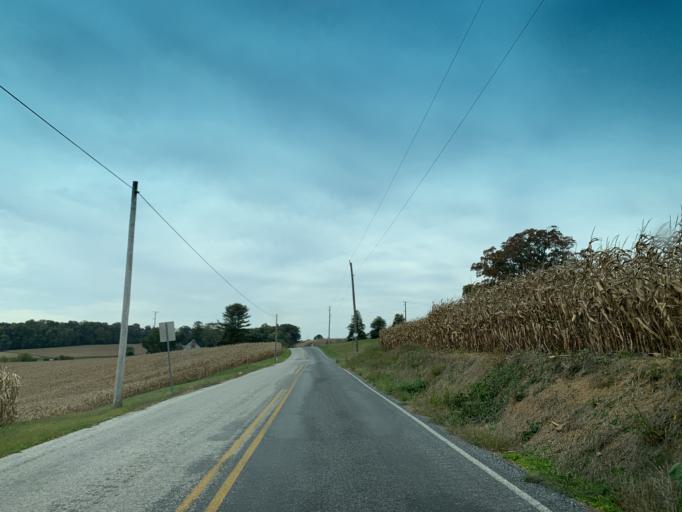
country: US
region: Pennsylvania
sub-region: York County
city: Stewartstown
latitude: 39.8050
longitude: -76.4971
